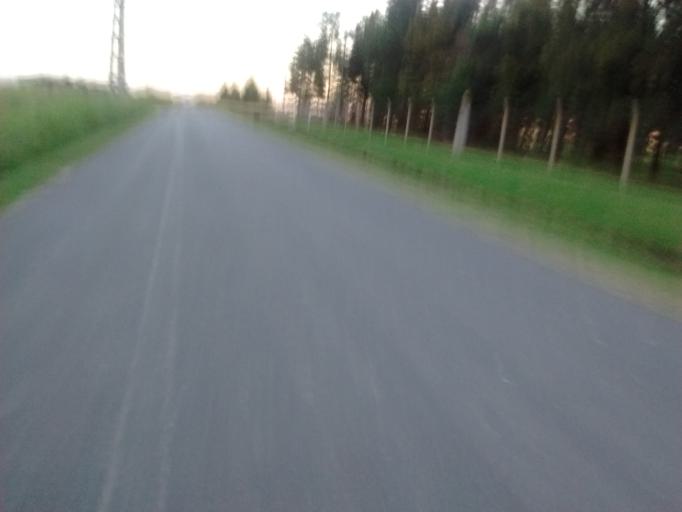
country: AR
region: Santa Fe
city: Funes
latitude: -32.9522
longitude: -60.8194
